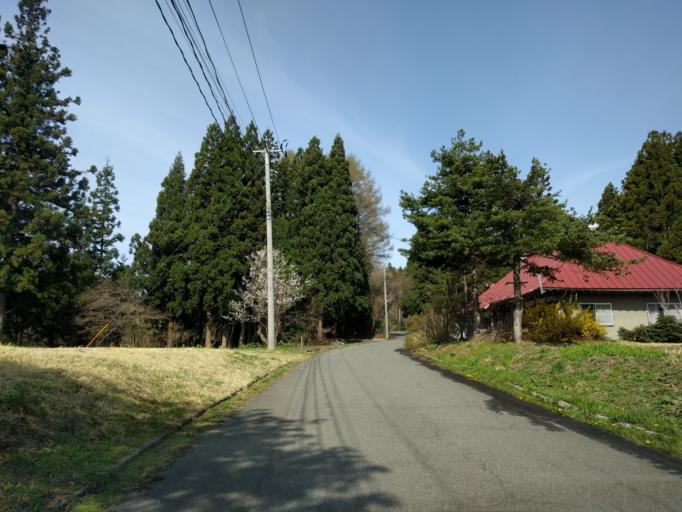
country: JP
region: Fukushima
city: Inawashiro
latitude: 37.5216
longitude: 140.0411
